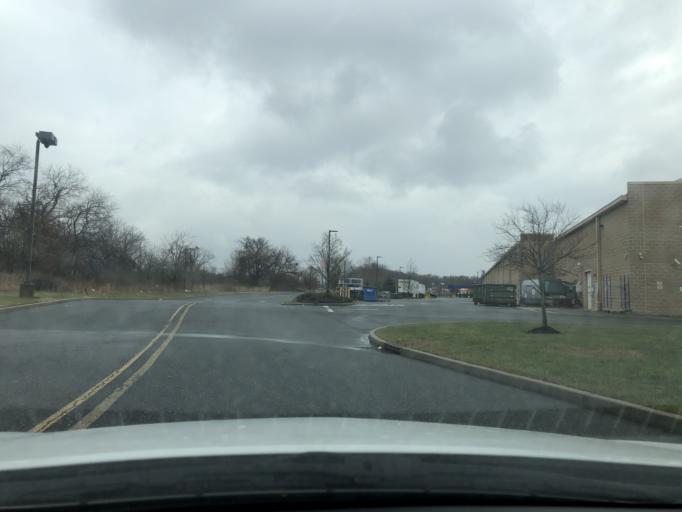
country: US
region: New Jersey
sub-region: Camden County
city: Glendora
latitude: 39.8407
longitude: -75.0896
